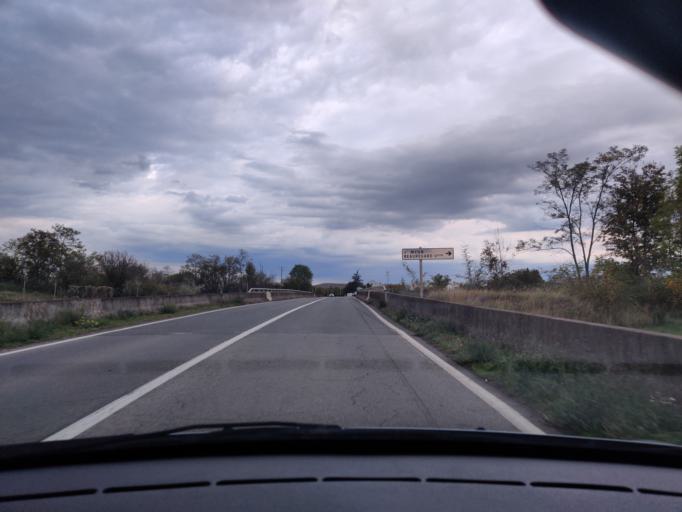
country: FR
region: Auvergne
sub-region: Departement du Puy-de-Dome
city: Saint-Bonnet-pres-Riom
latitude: 45.9530
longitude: 3.1066
